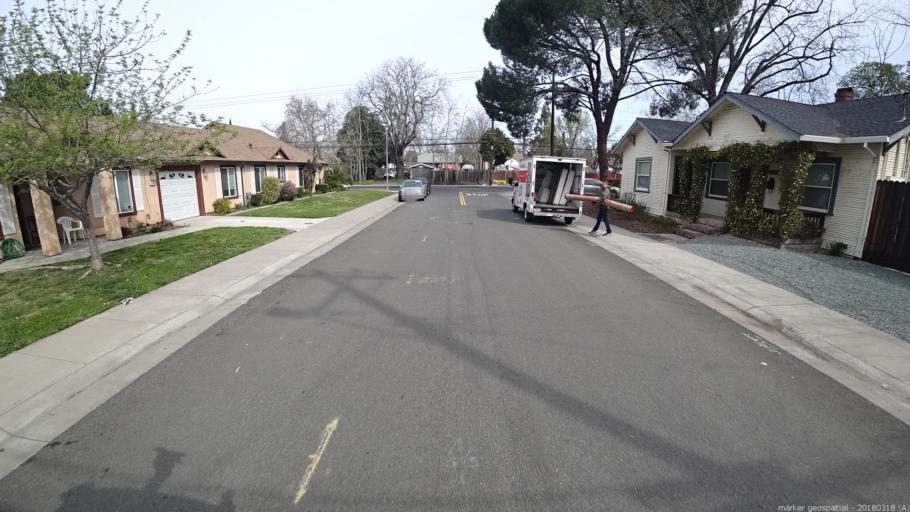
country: US
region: California
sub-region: Sacramento County
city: Parkway
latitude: 38.5391
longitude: -121.4475
